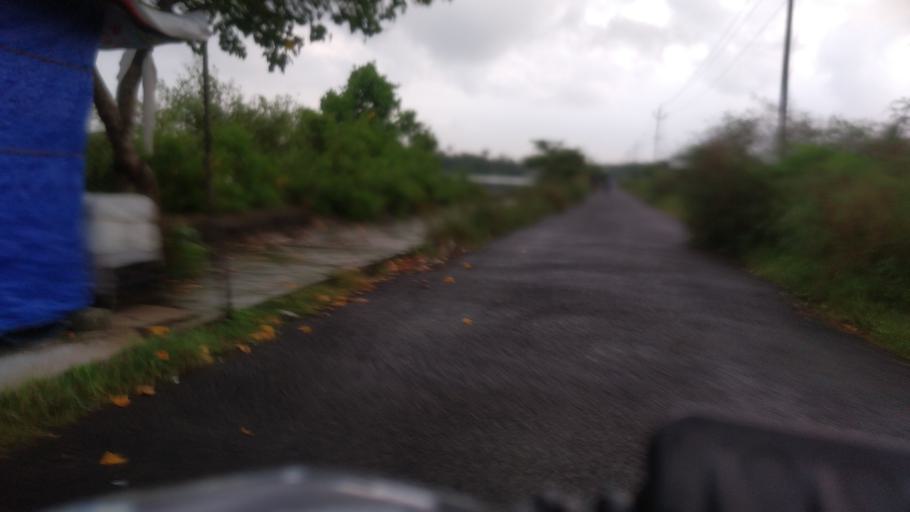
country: IN
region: Kerala
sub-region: Ernakulam
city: Elur
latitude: 10.0161
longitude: 76.2200
